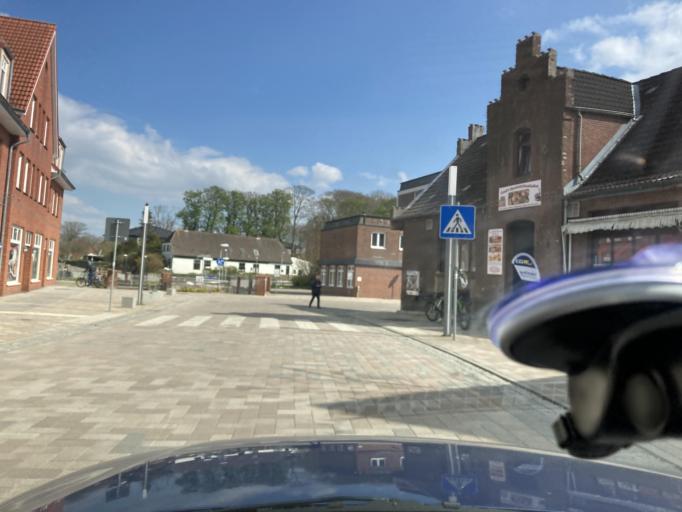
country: DE
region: Schleswig-Holstein
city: Meldorf
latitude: 54.0891
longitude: 9.0789
